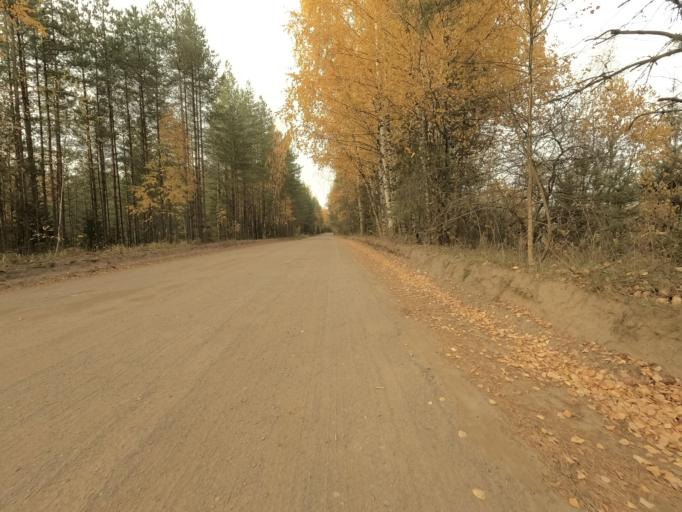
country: RU
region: Leningrad
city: Priladozhskiy
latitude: 59.6825
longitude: 31.3632
